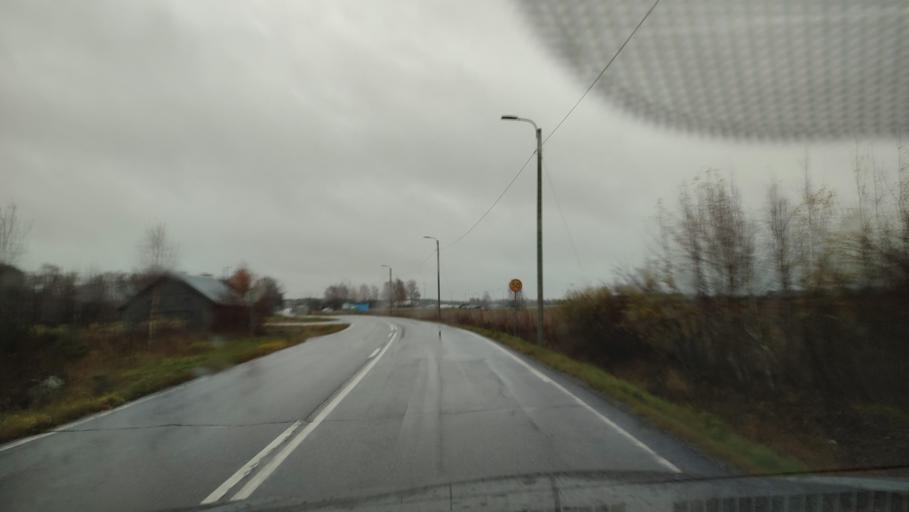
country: FI
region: Ostrobothnia
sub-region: Vaasa
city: Ristinummi
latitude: 63.0441
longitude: 21.7513
